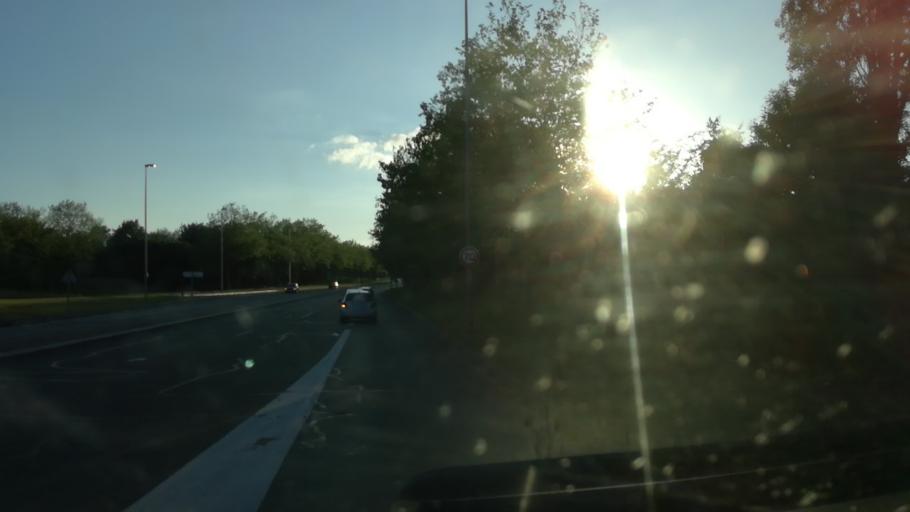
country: FR
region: Ile-de-France
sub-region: Departement des Yvelines
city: Elancourt
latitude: 48.7776
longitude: 1.9658
